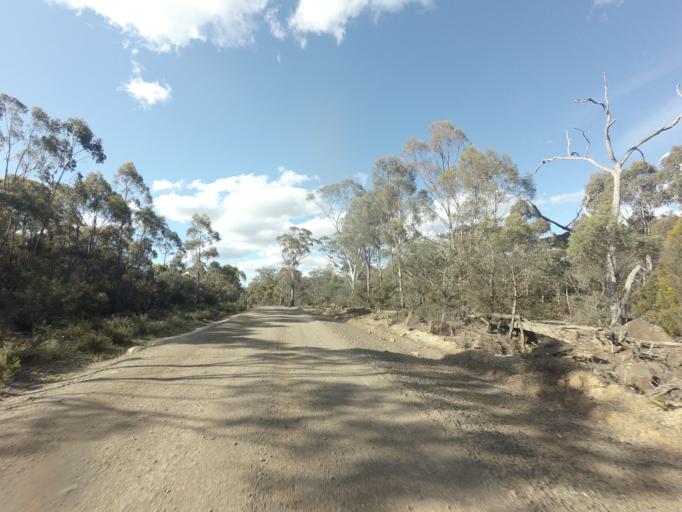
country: AU
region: Tasmania
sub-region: Break O'Day
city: St Helens
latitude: -41.8353
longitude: 148.0170
